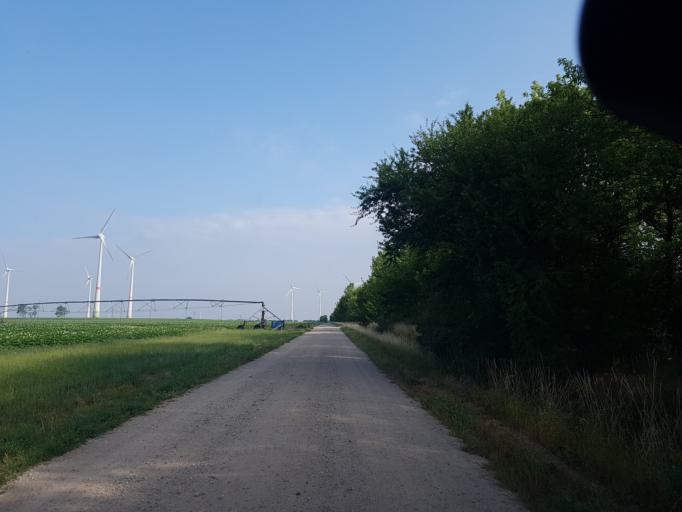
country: DE
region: Saxony-Anhalt
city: Kropstadt
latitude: 51.9854
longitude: 12.8215
